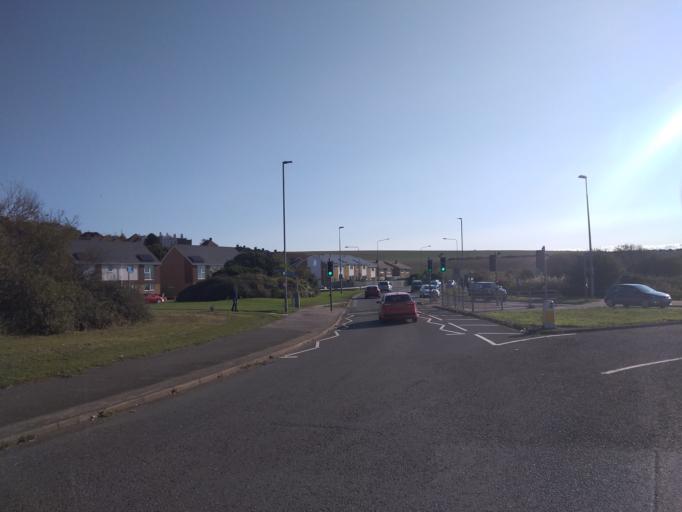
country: GB
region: England
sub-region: East Sussex
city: Newhaven
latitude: 50.7987
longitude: 0.0629
